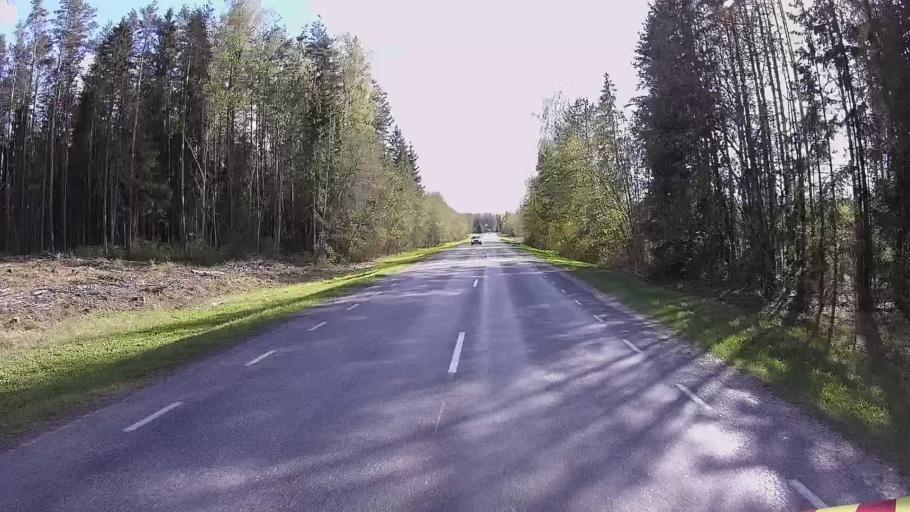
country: EE
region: Jogevamaa
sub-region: Jogeva linn
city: Jogeva
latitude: 58.7432
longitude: 26.3043
